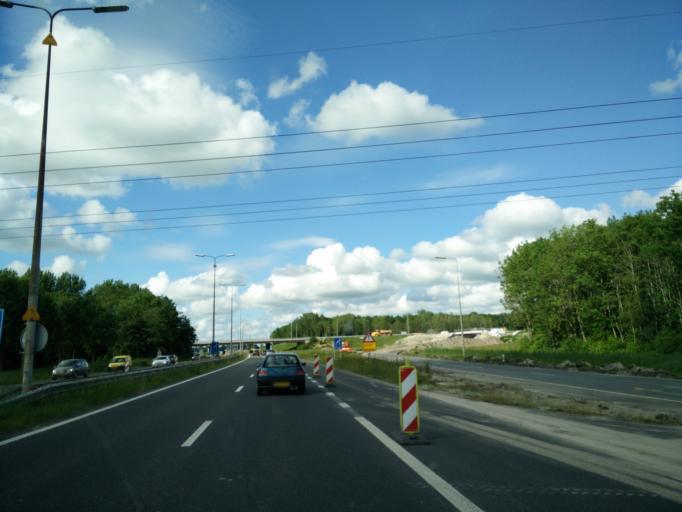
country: NL
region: Groningen
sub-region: Gemeente Groningen
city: Korrewegwijk
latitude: 53.2474
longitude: 6.5726
